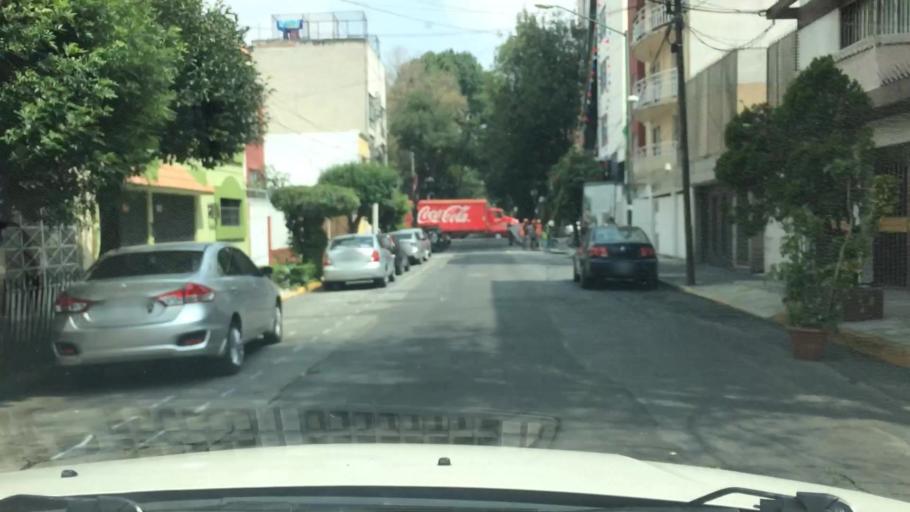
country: MX
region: Mexico City
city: Colonia del Valle
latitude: 19.3794
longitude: -99.1523
